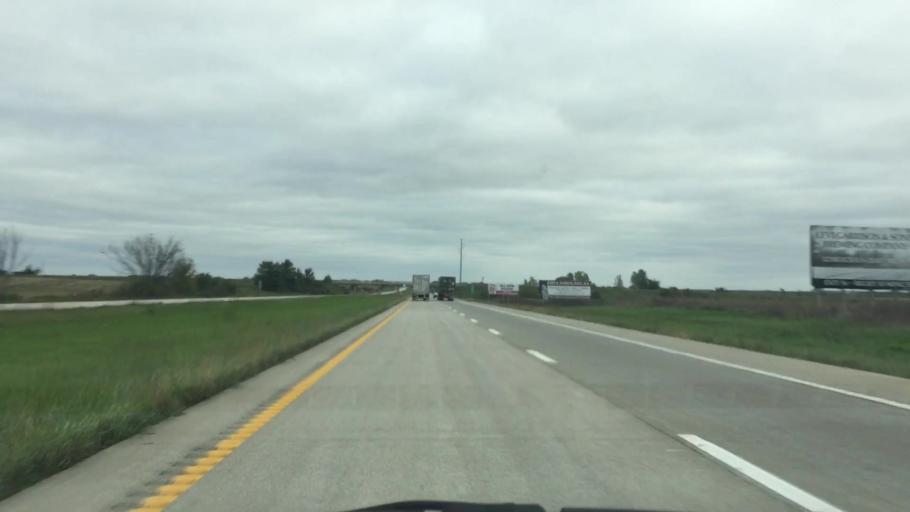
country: US
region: Missouri
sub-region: Clinton County
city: Cameron
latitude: 39.6290
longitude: -94.2453
